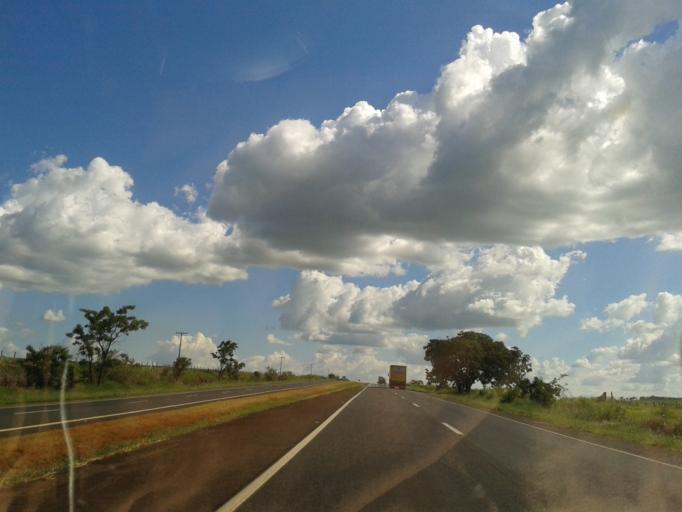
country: BR
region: Goias
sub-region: Goiatuba
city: Goiatuba
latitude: -18.1628
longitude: -49.2882
